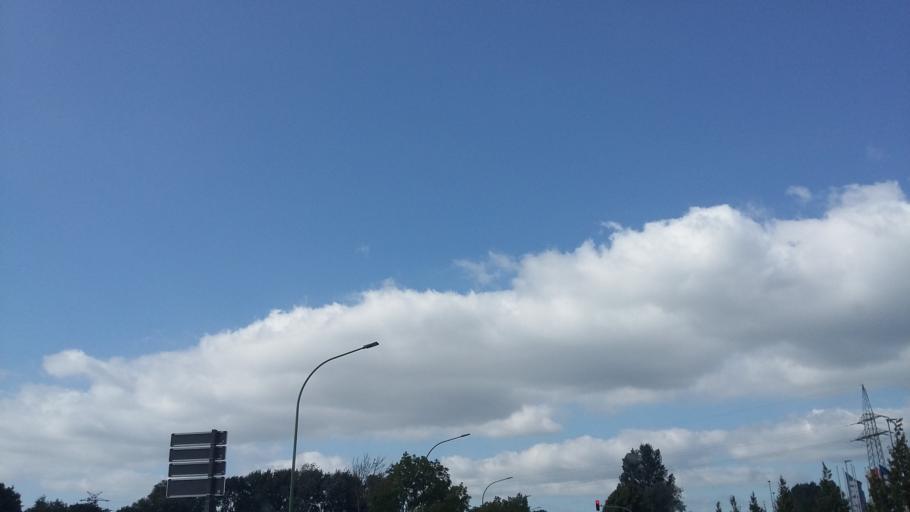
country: DE
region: Lower Saxony
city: Loxstedt
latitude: 53.4885
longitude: 8.6029
